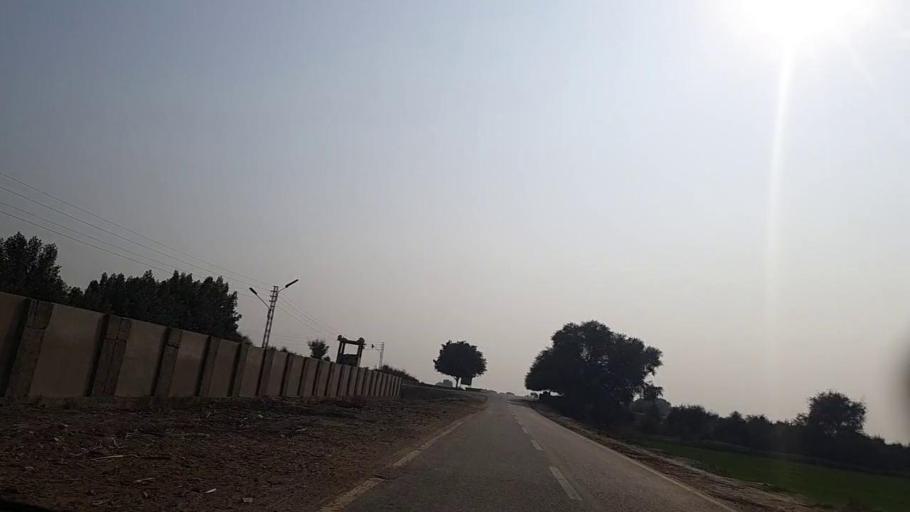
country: PK
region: Sindh
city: Sann
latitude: 26.1792
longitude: 68.1084
